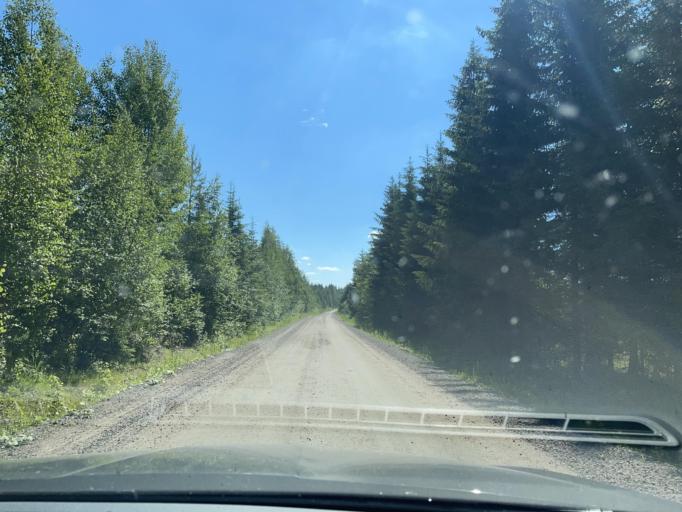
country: FI
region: Central Finland
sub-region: Saarijaervi-Viitasaari
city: Viitasaari
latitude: 63.2418
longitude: 25.9424
